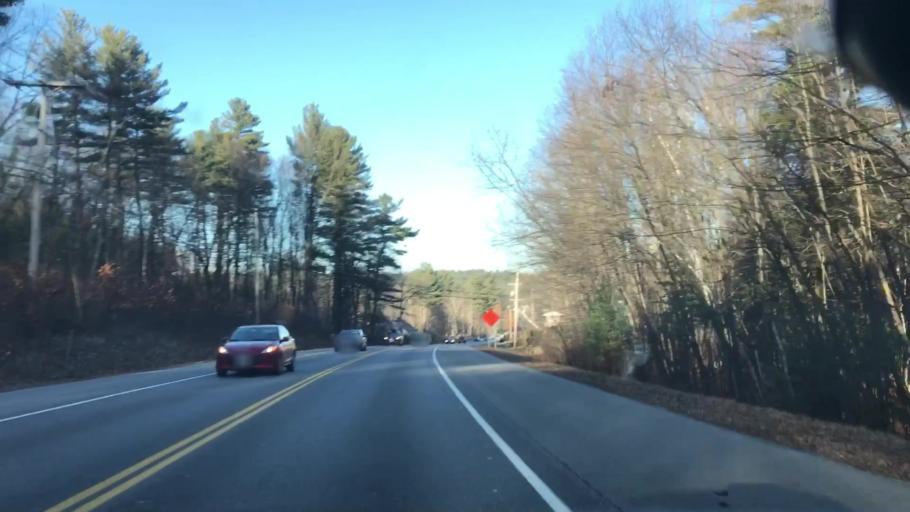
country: US
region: New Hampshire
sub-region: Hillsborough County
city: Bedford
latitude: 42.9327
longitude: -71.5311
